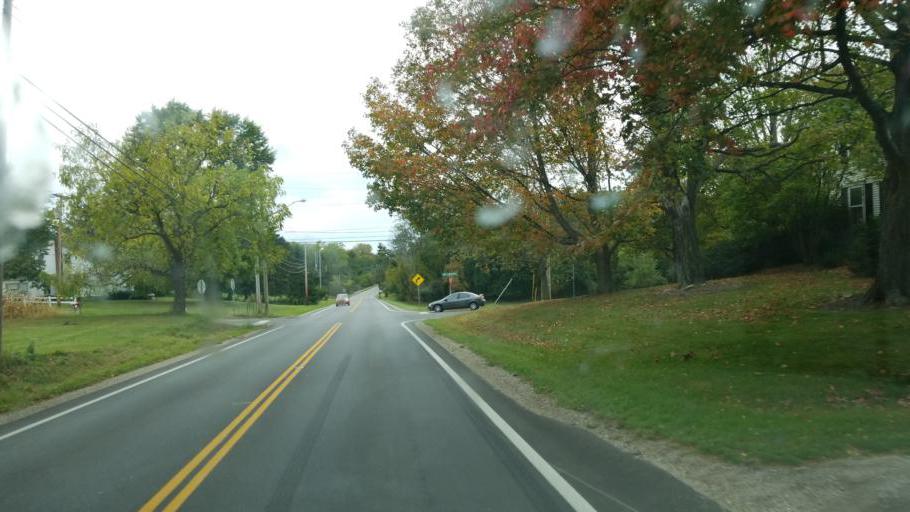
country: US
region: Ohio
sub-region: Lorain County
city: South Amherst
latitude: 41.3356
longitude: -82.3312
